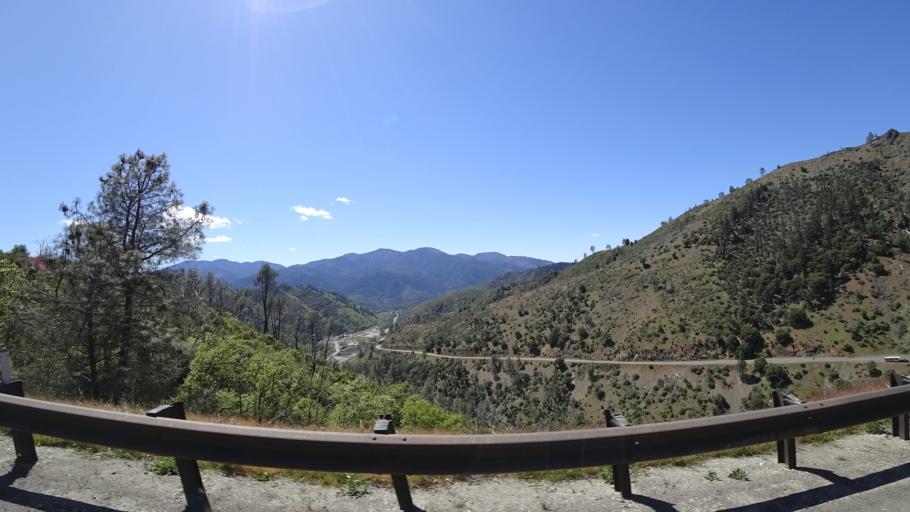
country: US
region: California
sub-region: Trinity County
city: Weaverville
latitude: 40.7384
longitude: -123.0009
